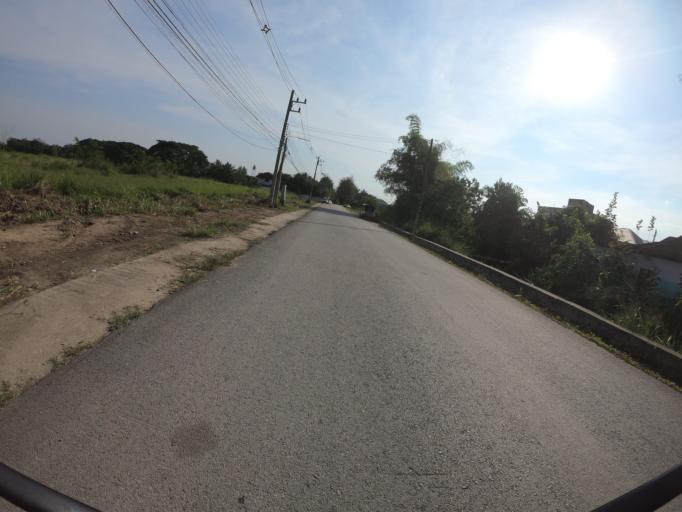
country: TH
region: Chiang Mai
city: Chiang Mai
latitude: 18.8486
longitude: 98.9802
